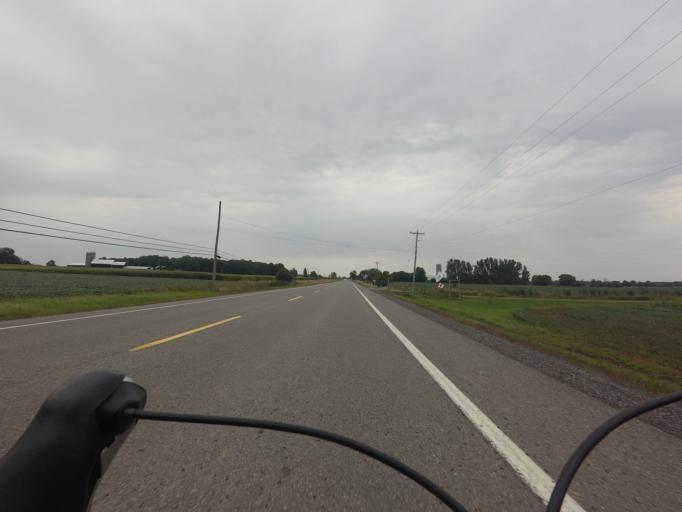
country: CA
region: Ontario
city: Bells Corners
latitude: 45.1520
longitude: -75.7417
